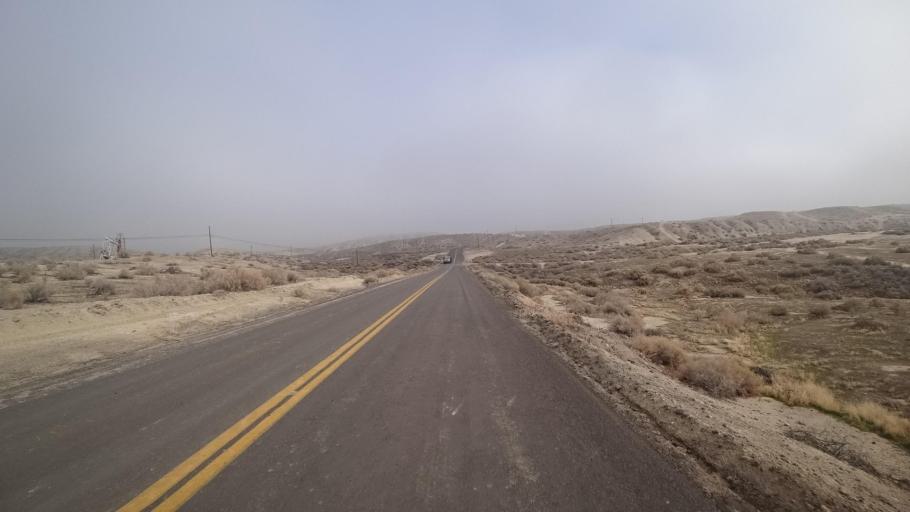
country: US
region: California
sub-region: Kern County
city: Ford City
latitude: 35.1659
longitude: -119.3972
